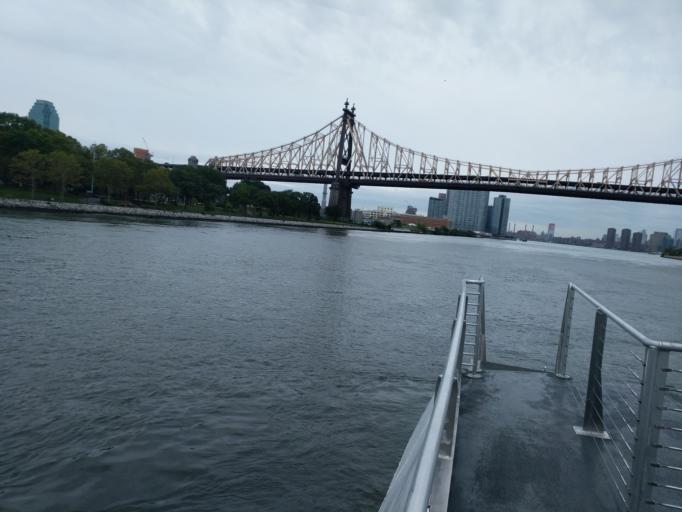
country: US
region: New York
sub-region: Queens County
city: Long Island City
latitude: 40.7590
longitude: -73.9494
